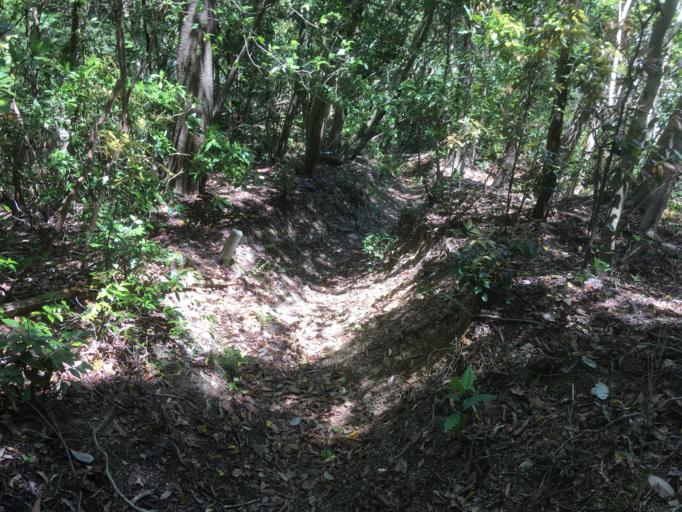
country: JP
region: Nara
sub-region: Ikoma-shi
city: Ikoma
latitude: 34.6932
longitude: 135.6888
